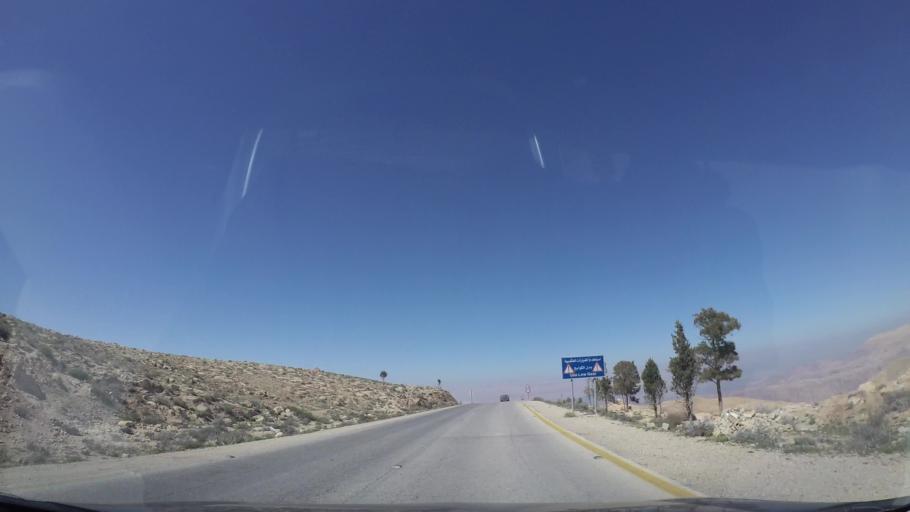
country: JO
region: Tafielah
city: At Tafilah
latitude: 30.8592
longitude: 35.5404
